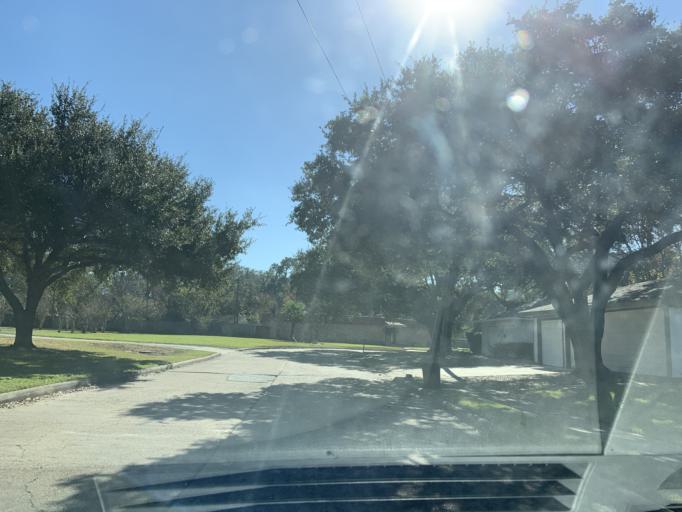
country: US
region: Texas
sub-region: Fort Bend County
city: Missouri City
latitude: 29.6728
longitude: -95.5155
